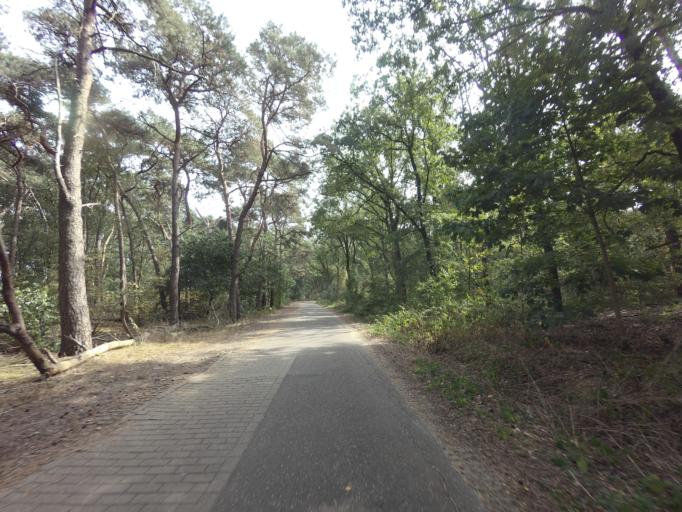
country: NL
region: North Brabant
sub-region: Gemeente Helmond
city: Helmond
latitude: 51.4801
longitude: 5.7165
